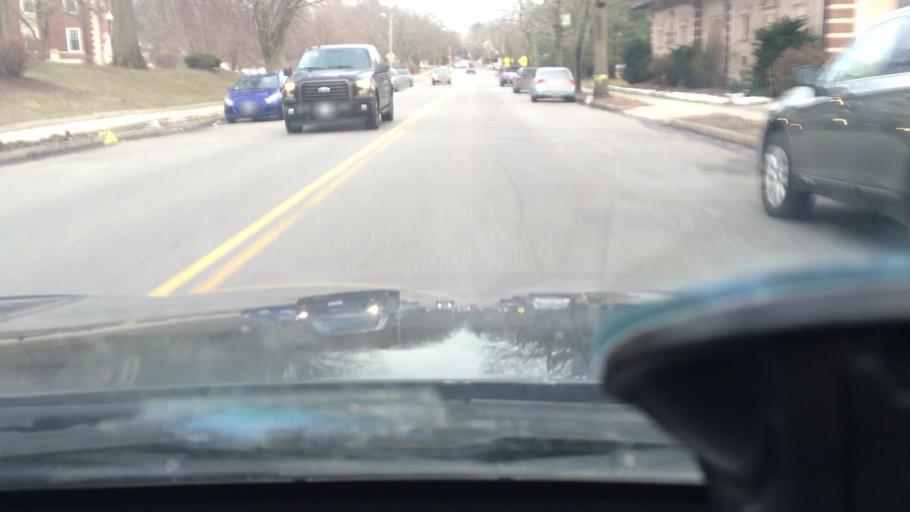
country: US
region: Massachusetts
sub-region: Middlesex County
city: Newton
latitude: 42.3371
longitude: -71.2101
